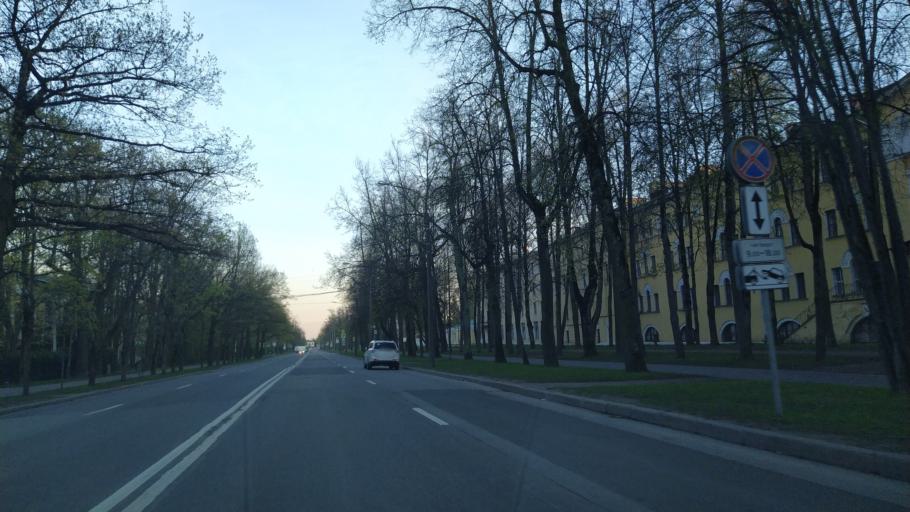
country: RU
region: St.-Petersburg
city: Pushkin
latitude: 59.7096
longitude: 30.4028
